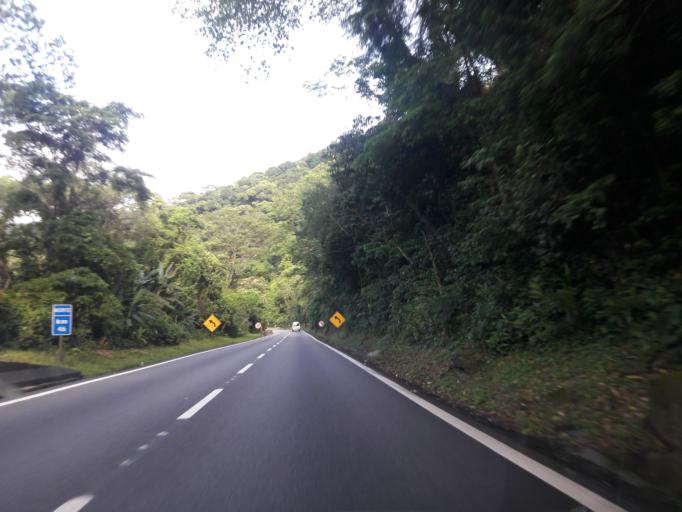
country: BR
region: Sao Paulo
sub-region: Cubatao
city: Cubatao
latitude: -23.8889
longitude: -46.4864
